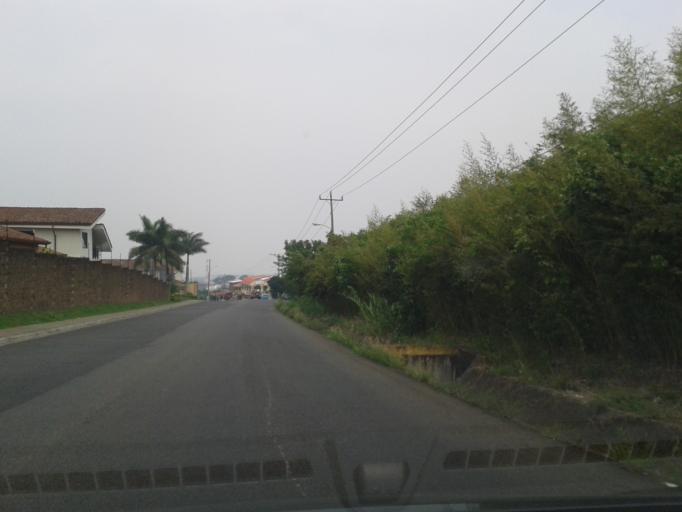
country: CR
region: Heredia
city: San Francisco
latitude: 9.9817
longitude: -84.1353
